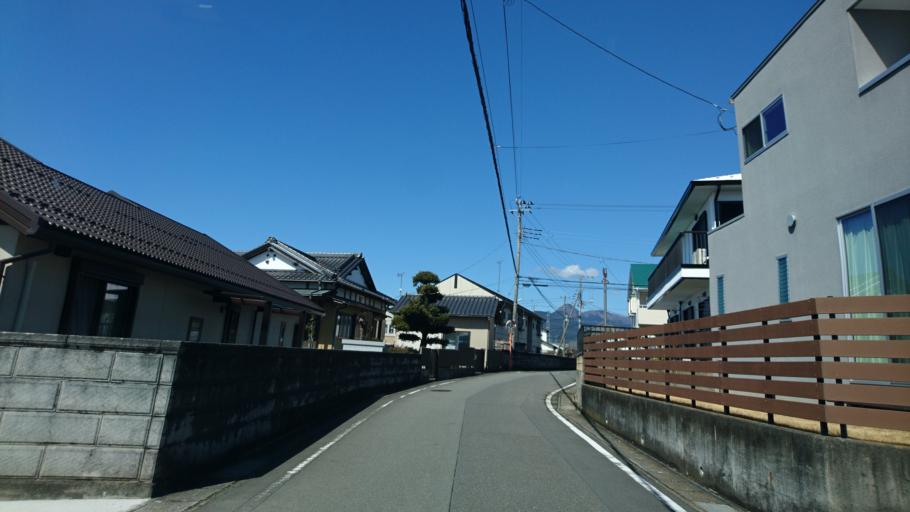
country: JP
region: Shizuoka
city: Fujinomiya
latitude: 35.2480
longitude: 138.6147
